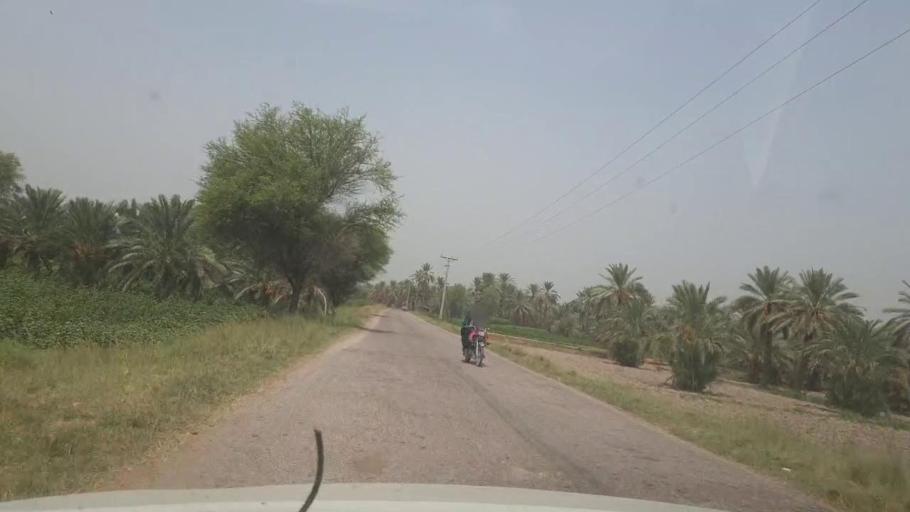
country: PK
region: Sindh
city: Kot Diji
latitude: 27.3624
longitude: 68.6809
